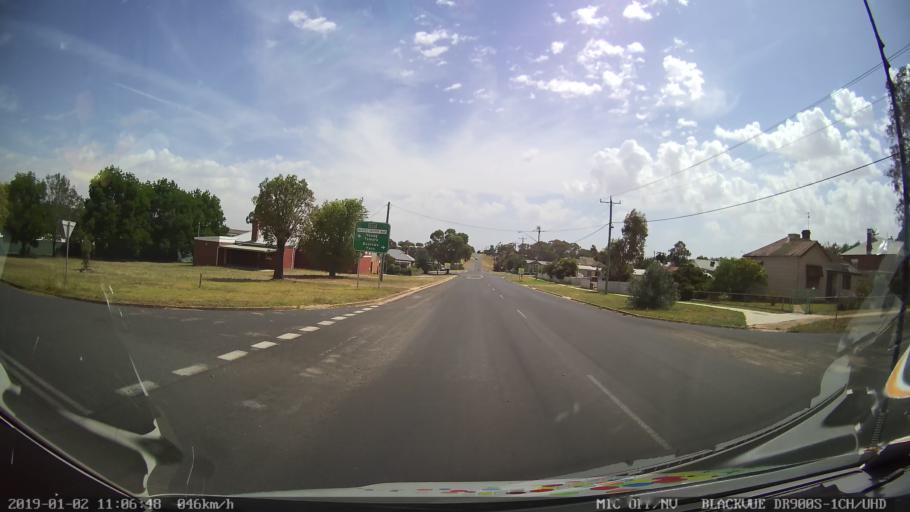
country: AU
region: New South Wales
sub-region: Young
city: Young
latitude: -34.5529
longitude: 148.3575
